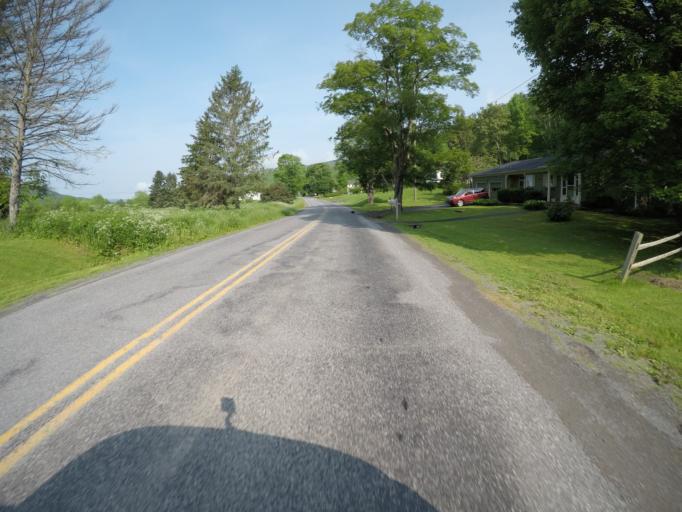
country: US
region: New York
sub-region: Sullivan County
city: Livingston Manor
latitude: 42.1265
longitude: -74.6873
